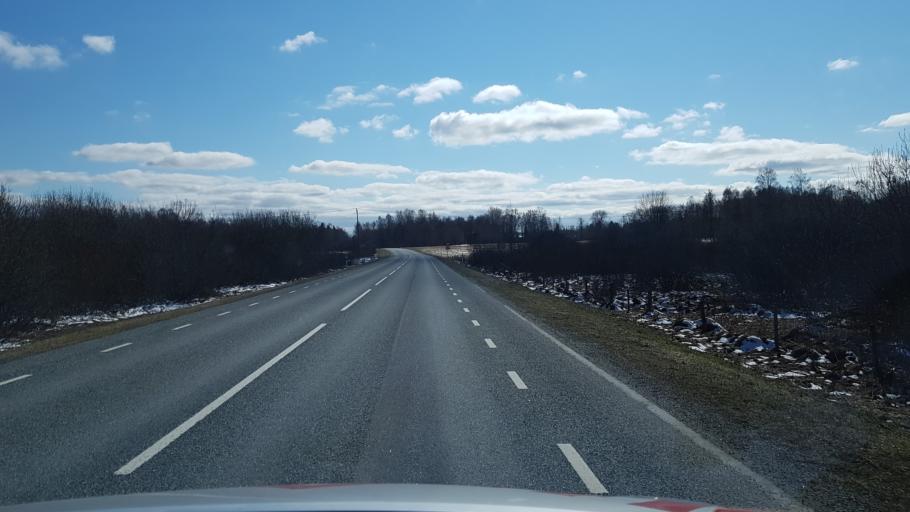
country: EE
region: Laeaene-Virumaa
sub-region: Tapa vald
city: Tapa
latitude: 59.4477
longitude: 25.9487
